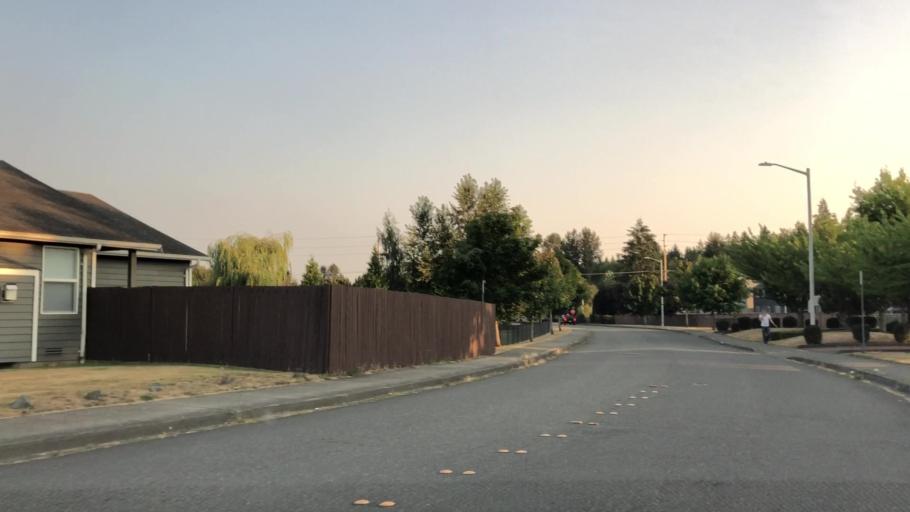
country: US
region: Washington
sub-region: Snohomish County
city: Marysville
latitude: 48.0870
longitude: -122.1499
